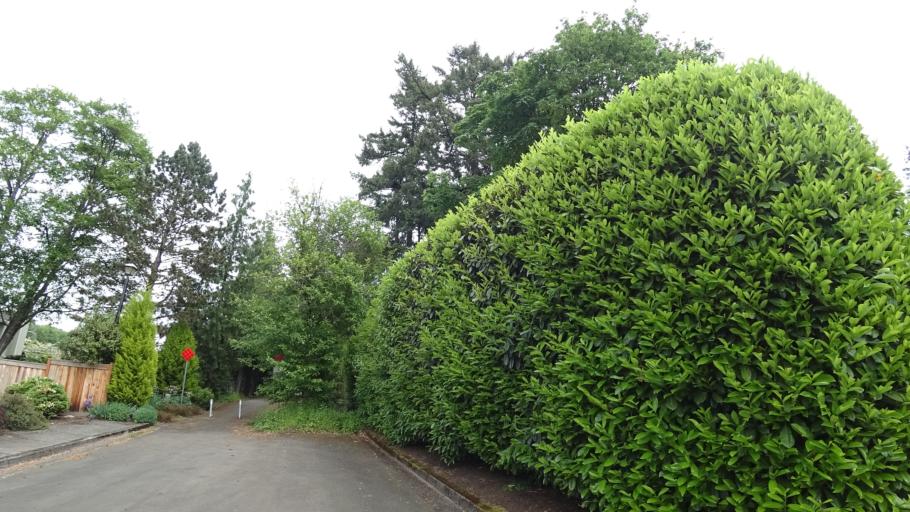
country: US
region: Oregon
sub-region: Washington County
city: Cedar Hills
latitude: 45.5019
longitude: -122.7846
